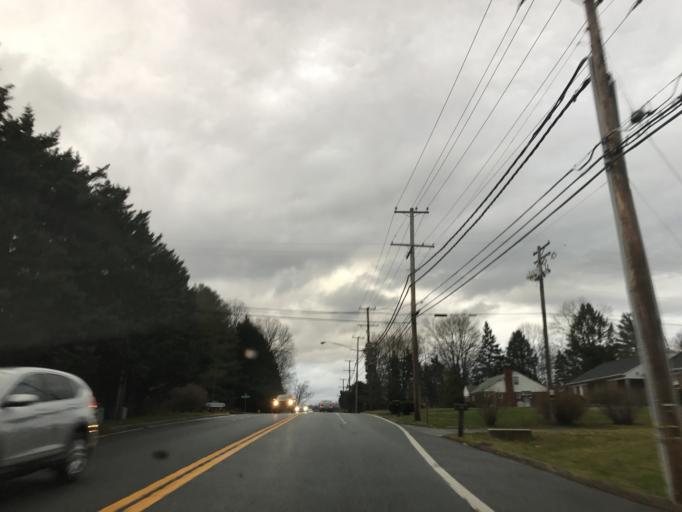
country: US
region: Maryland
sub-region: Harford County
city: South Bel Air
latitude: 39.5533
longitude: -76.3230
